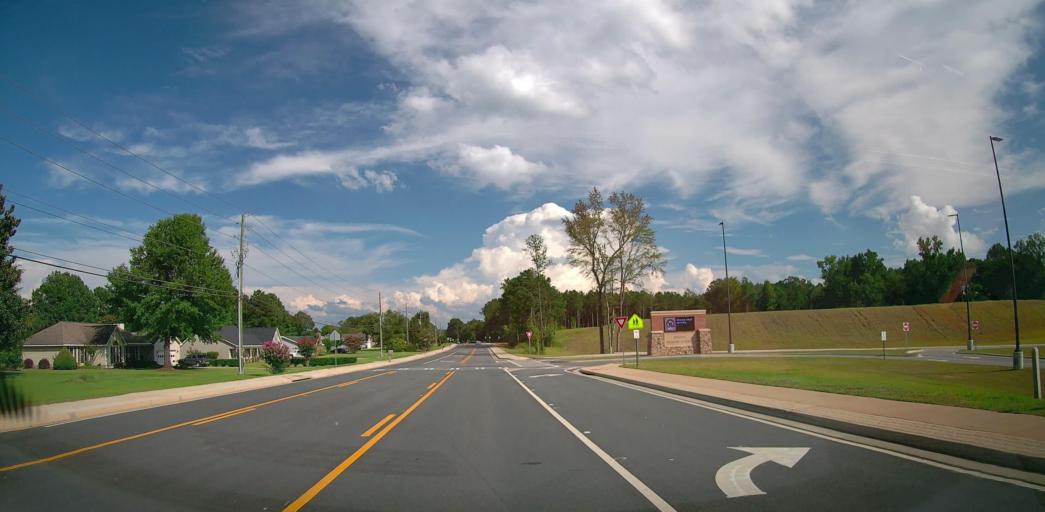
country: US
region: Georgia
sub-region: Houston County
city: Robins Air Force Base
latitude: 32.5381
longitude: -83.5696
